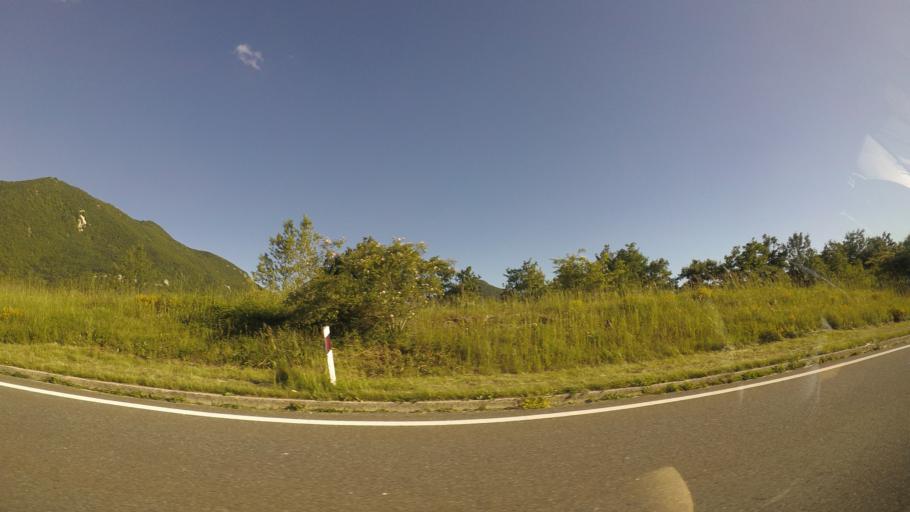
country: HR
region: Zadarska
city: Gracac
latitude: 44.4635
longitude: 15.6881
